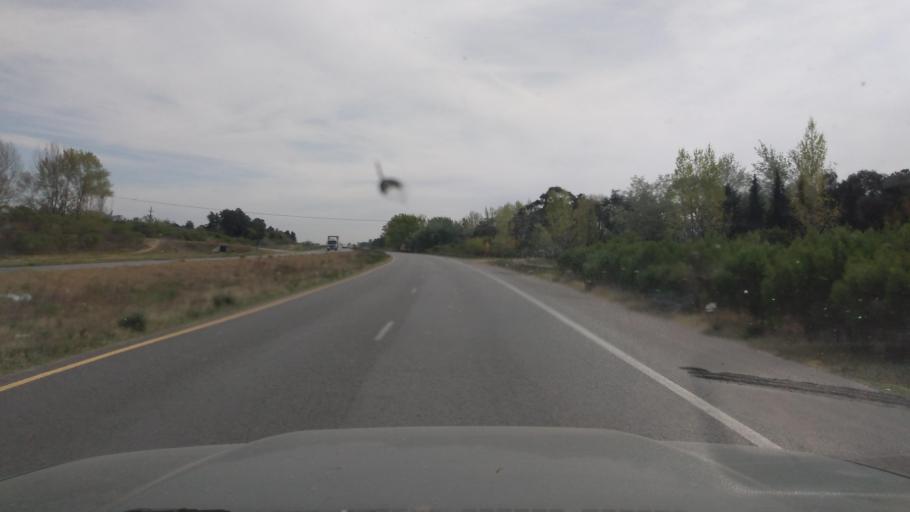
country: AR
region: Buenos Aires
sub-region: Partido de Lujan
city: Lujan
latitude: -34.4914
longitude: -59.0532
